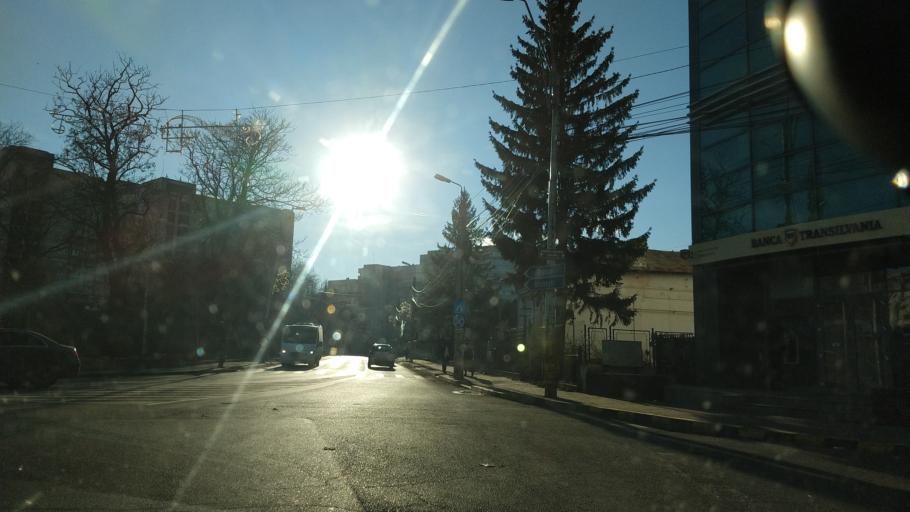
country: RO
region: Bacau
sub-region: Municipiul Bacau
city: Bacau
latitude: 46.5694
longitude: 26.9106
